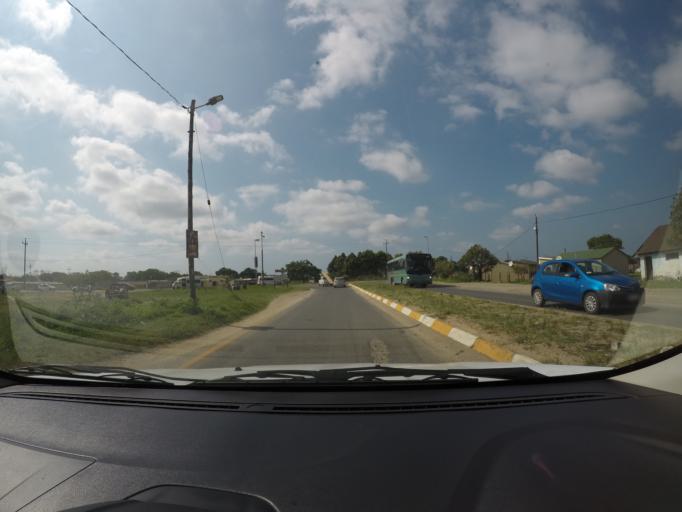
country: ZA
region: KwaZulu-Natal
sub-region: uThungulu District Municipality
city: eSikhawini
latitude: -28.8828
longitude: 31.9030
